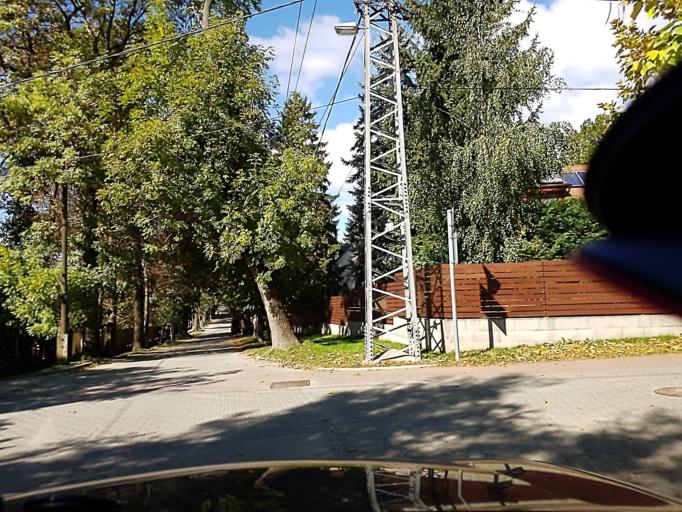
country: HU
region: Pest
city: Piliscsaba
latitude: 47.6386
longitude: 18.8431
